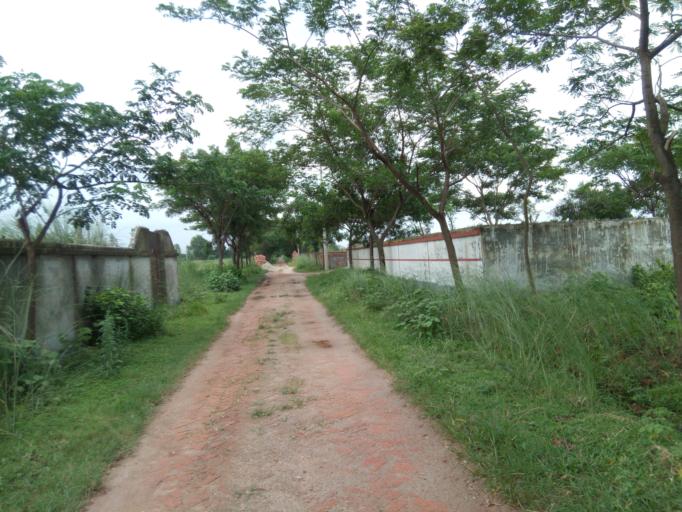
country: BD
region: Dhaka
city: Azimpur
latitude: 23.7530
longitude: 90.3348
